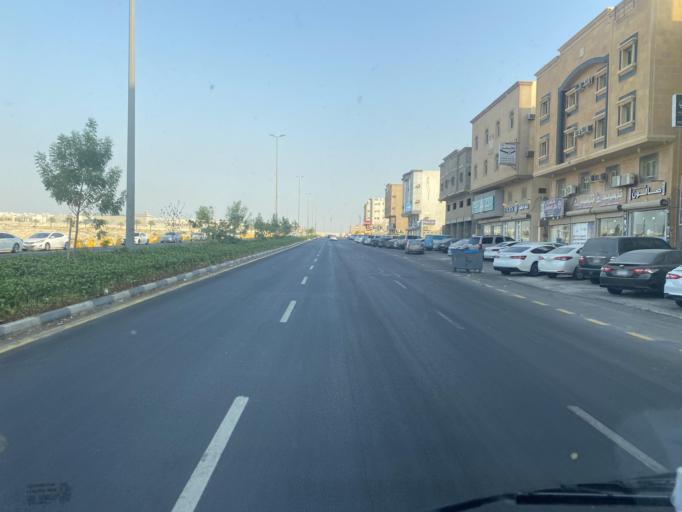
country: SA
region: Eastern Province
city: Dhahran
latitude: 26.3527
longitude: 50.0494
